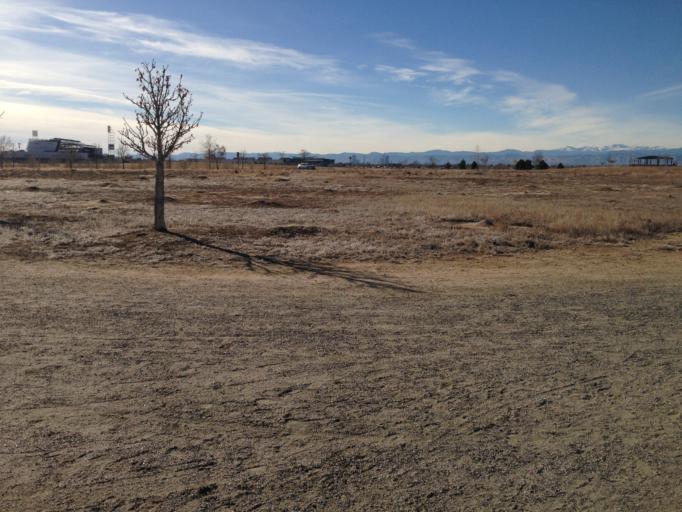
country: US
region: Colorado
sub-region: Adams County
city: Derby
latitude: 39.8128
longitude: -104.8887
